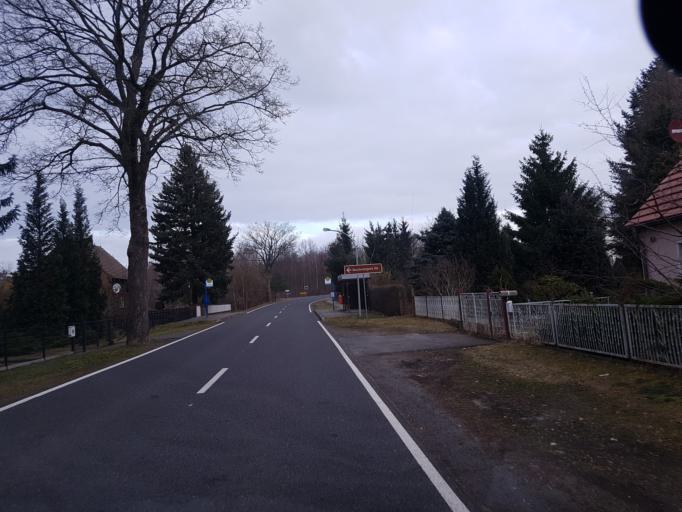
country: DE
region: Brandenburg
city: Sallgast
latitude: 51.5789
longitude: 13.8493
